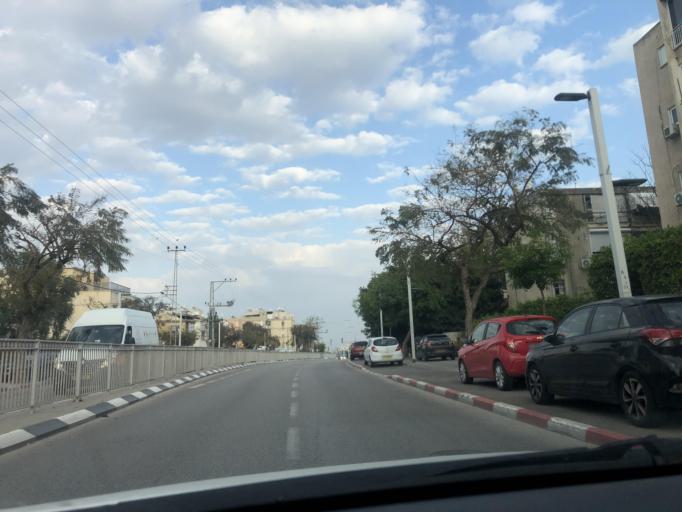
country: IL
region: Tel Aviv
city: Bat Yam
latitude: 32.0235
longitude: 34.7559
